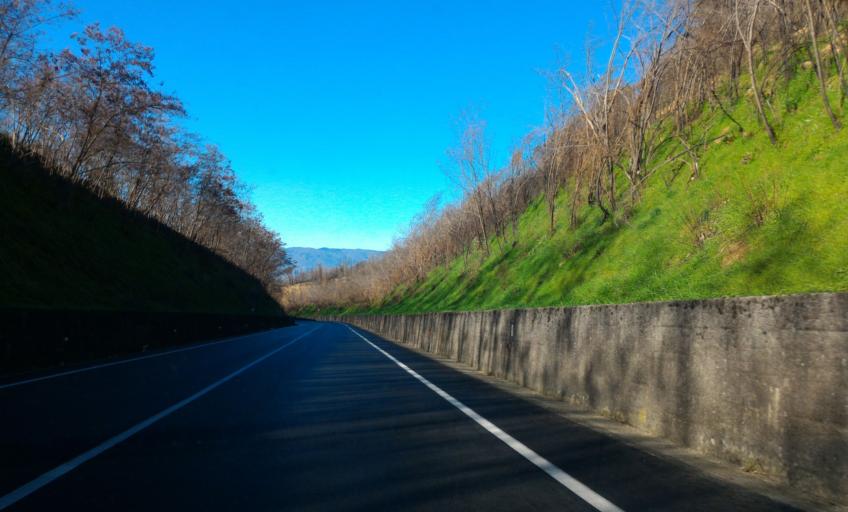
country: IT
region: Calabria
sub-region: Provincia di Cosenza
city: Zumpano
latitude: 39.2974
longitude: 16.3018
